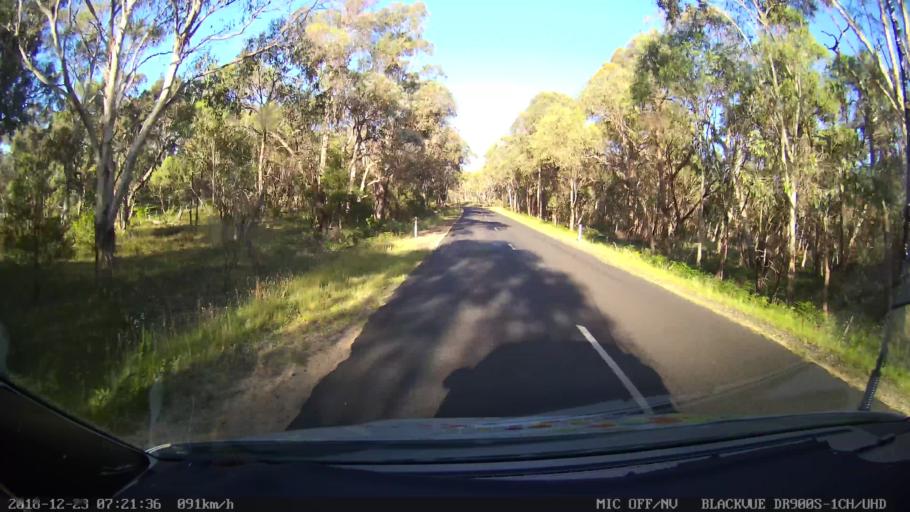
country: AU
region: New South Wales
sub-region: Bellingen
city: Dorrigo
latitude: -30.4974
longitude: 152.2608
